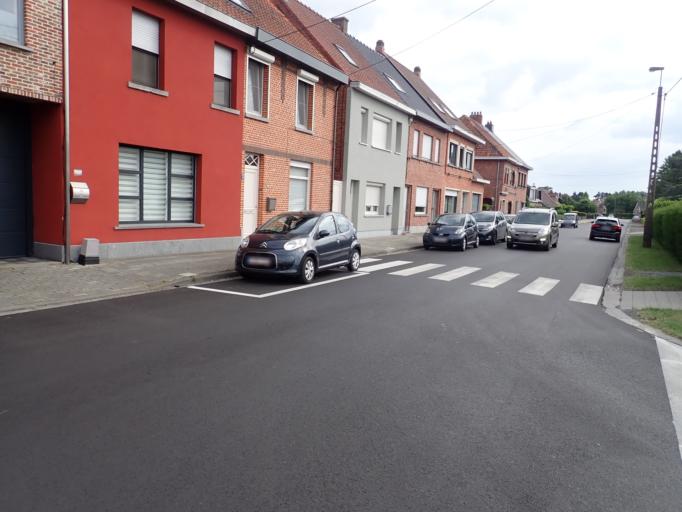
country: BE
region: Flanders
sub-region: Provincie Oost-Vlaanderen
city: Hamme
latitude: 51.0916
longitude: 4.1201
